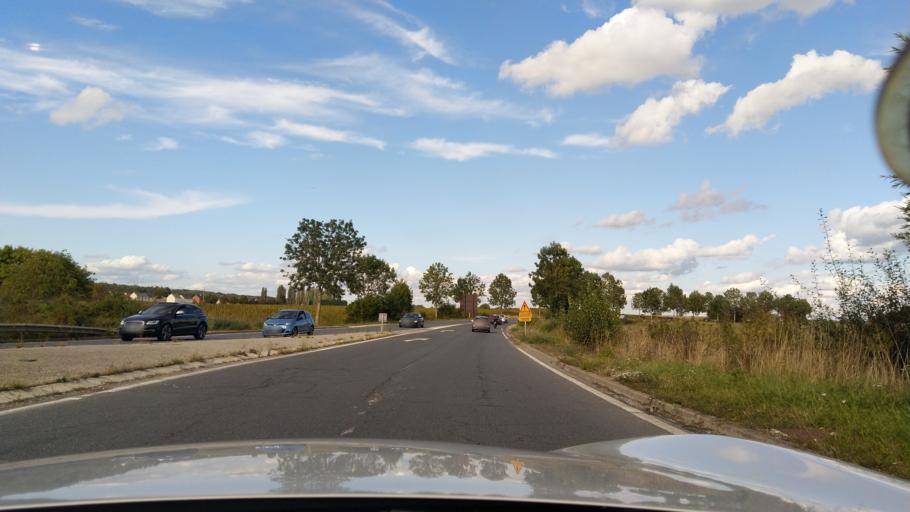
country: FR
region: Ile-de-France
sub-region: Departement de Seine-et-Marne
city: Cregy-les-Meaux
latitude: 48.9789
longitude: 2.8638
